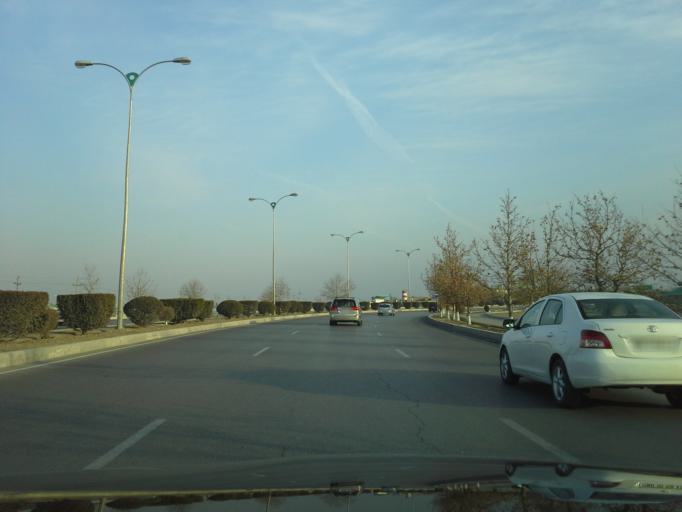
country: TM
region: Ahal
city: Abadan
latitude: 38.0561
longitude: 58.1809
